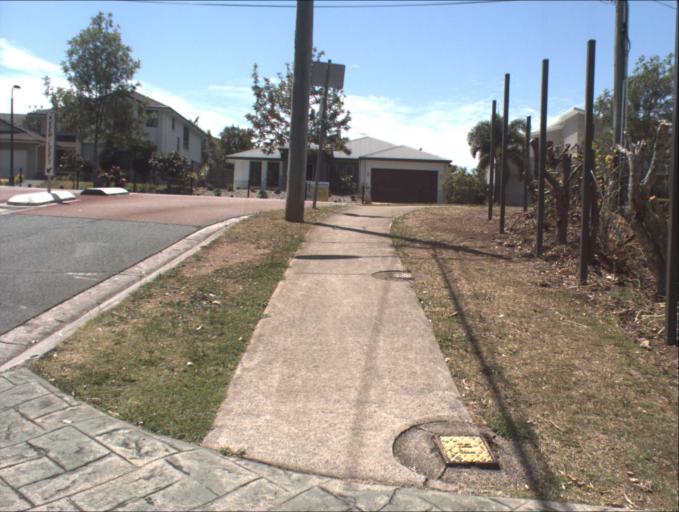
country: AU
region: Queensland
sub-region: Logan
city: Slacks Creek
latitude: -27.6352
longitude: 153.1547
